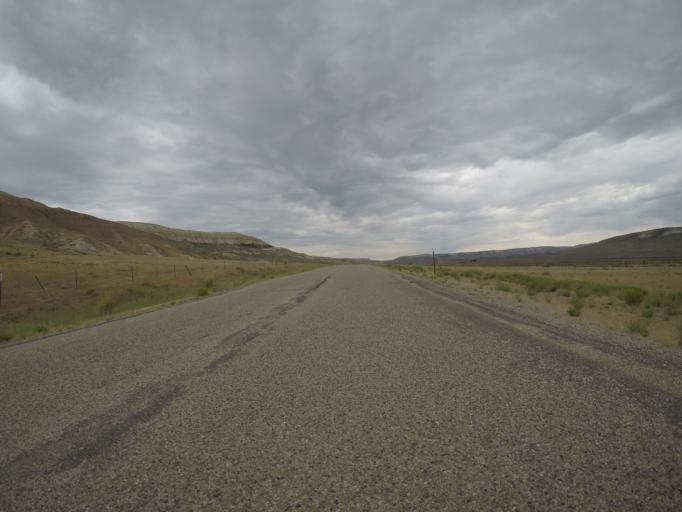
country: US
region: Wyoming
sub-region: Lincoln County
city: Kemmerer
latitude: 41.8231
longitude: -110.7445
